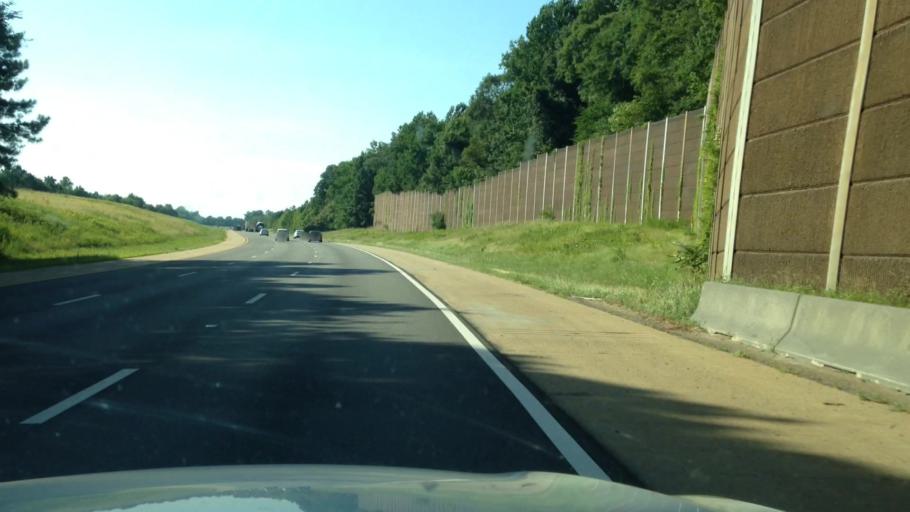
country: US
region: Virginia
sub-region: Chesterfield County
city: Enon
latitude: 37.2919
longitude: -77.3289
